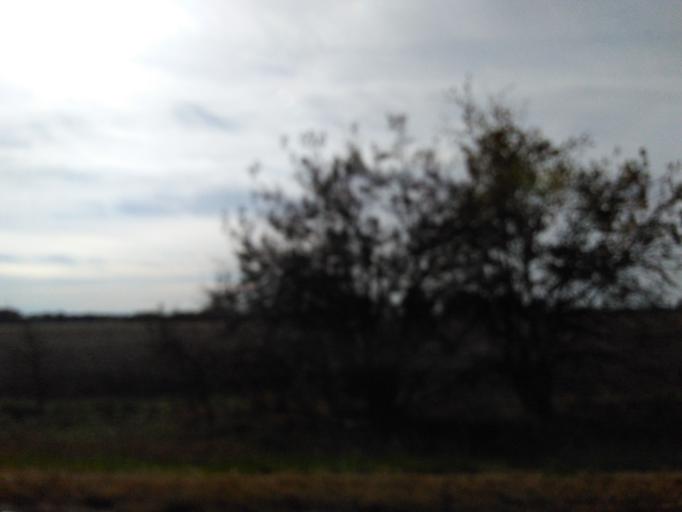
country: US
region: Illinois
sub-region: Madison County
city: Highland
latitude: 38.7844
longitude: -89.7272
